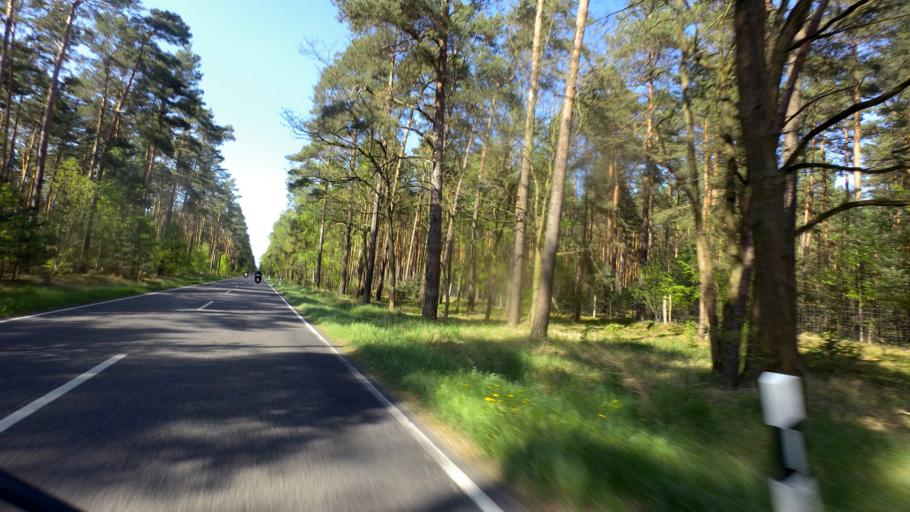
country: DE
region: Brandenburg
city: Gross Koris
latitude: 52.2018
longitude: 13.6932
